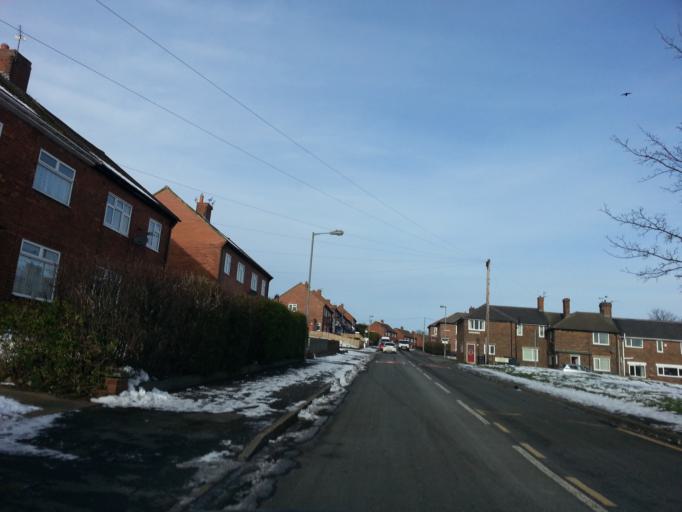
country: GB
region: England
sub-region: County Durham
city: Crook
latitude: 54.7142
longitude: -1.7553
